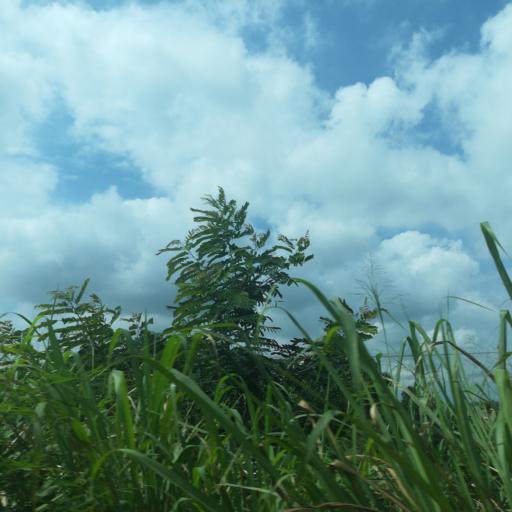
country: NG
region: Ogun
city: Odogbolu
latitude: 6.6512
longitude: 3.7051
